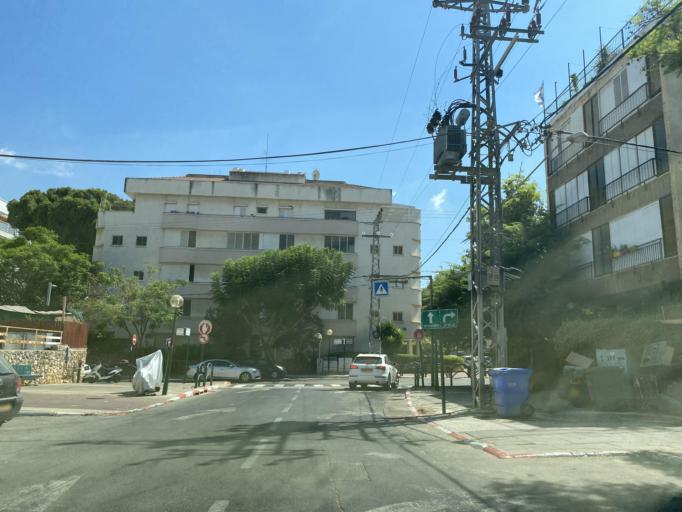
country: IL
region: Central District
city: Kfar Saba
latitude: 32.1735
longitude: 34.9051
